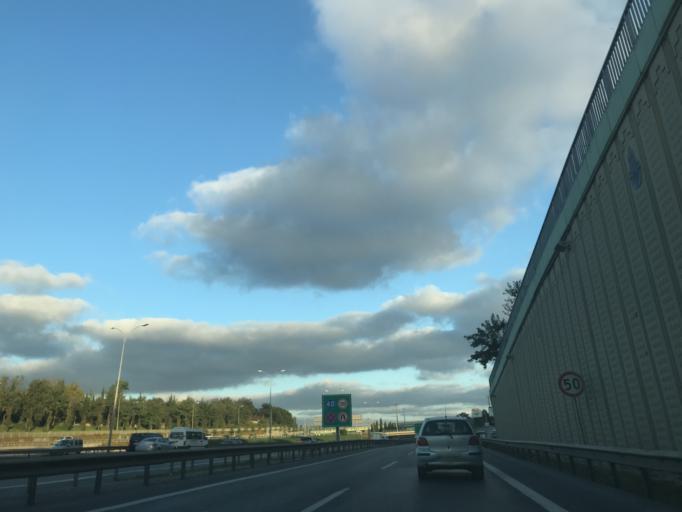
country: TR
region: Istanbul
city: Sisli
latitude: 41.1006
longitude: 29.0028
